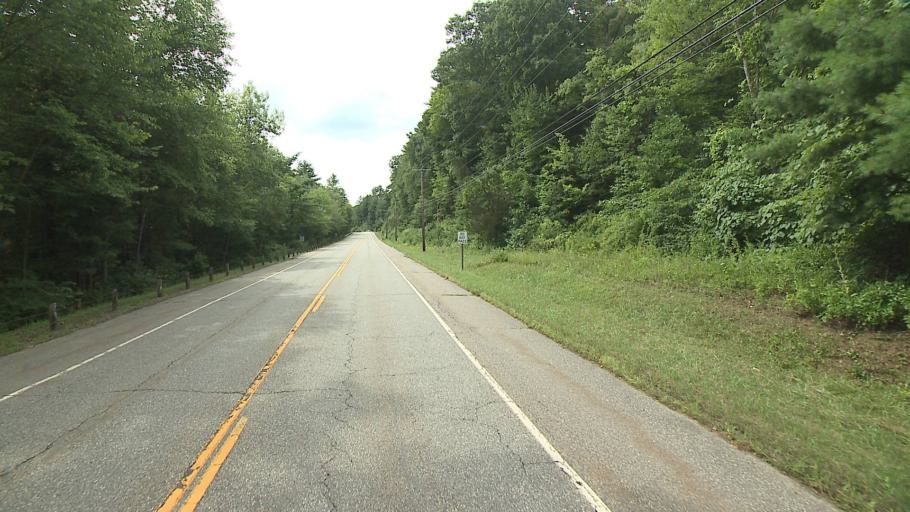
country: US
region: Connecticut
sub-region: Litchfield County
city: New Preston
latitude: 41.6718
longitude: -73.3243
